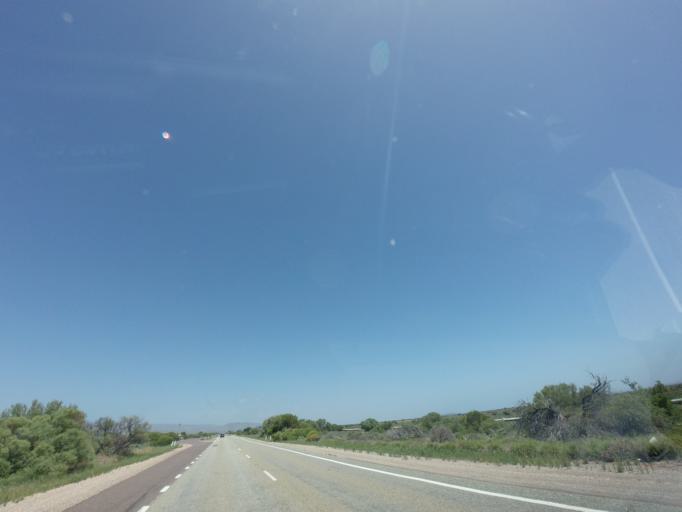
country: AU
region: South Australia
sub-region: Port Augusta
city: Port Augusta
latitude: -32.6211
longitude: 137.9115
